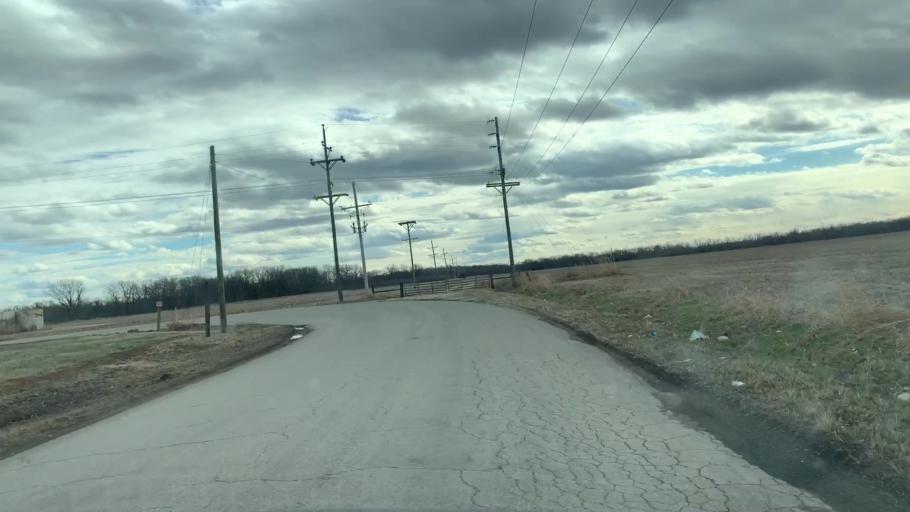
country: US
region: Kansas
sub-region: Allen County
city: Humboldt
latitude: 37.8115
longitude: -95.4525
